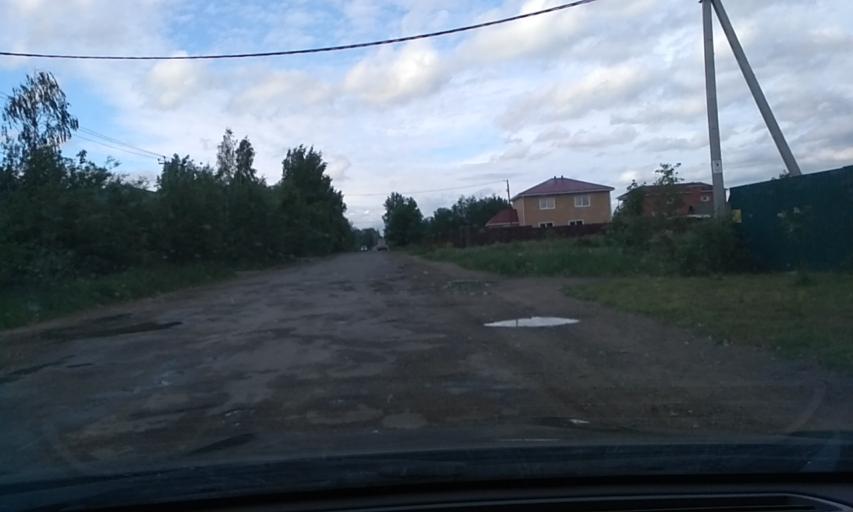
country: RU
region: Leningrad
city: Otradnoye
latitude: 59.7905
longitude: 30.7925
